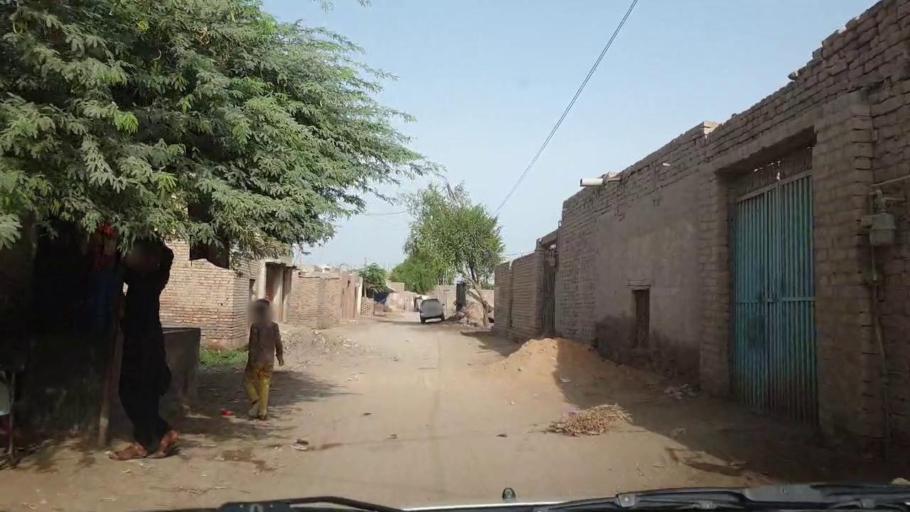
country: PK
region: Sindh
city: Nawabshah
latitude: 26.2299
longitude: 68.4117
